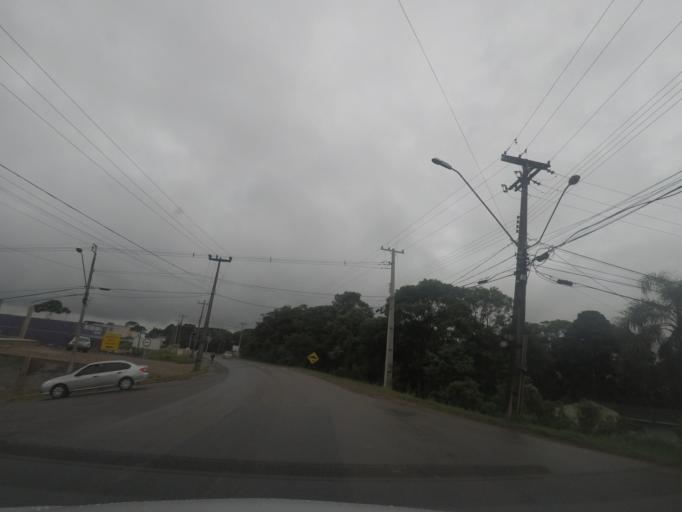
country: BR
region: Parana
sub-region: Quatro Barras
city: Quatro Barras
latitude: -25.3436
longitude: -49.0841
